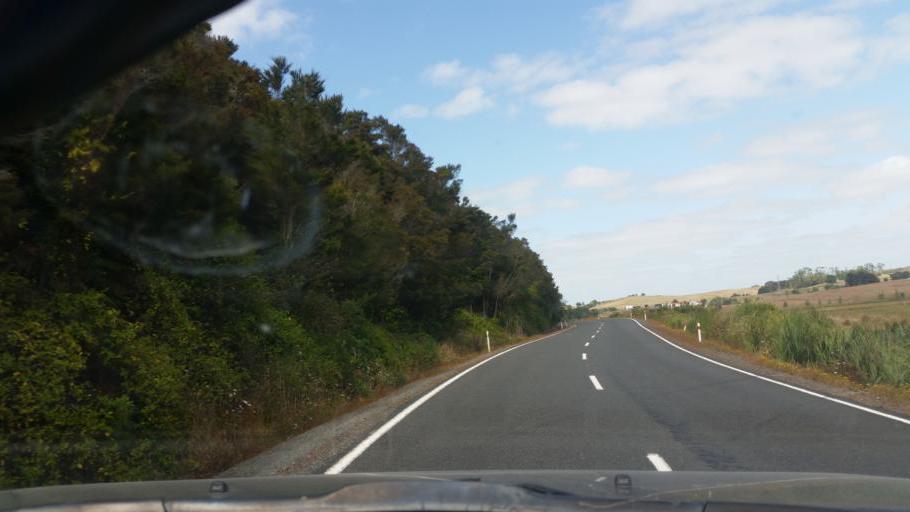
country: NZ
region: Northland
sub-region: Whangarei
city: Ruakaka
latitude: -35.9669
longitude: 174.2911
